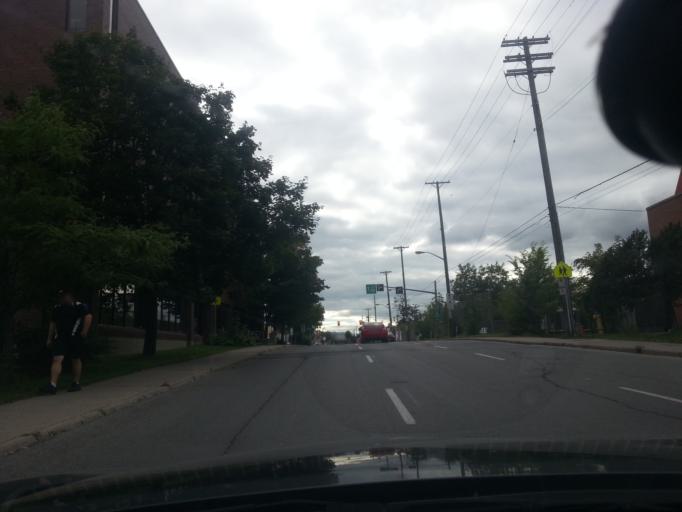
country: CA
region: Ontario
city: Ottawa
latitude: 45.4094
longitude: -75.6924
